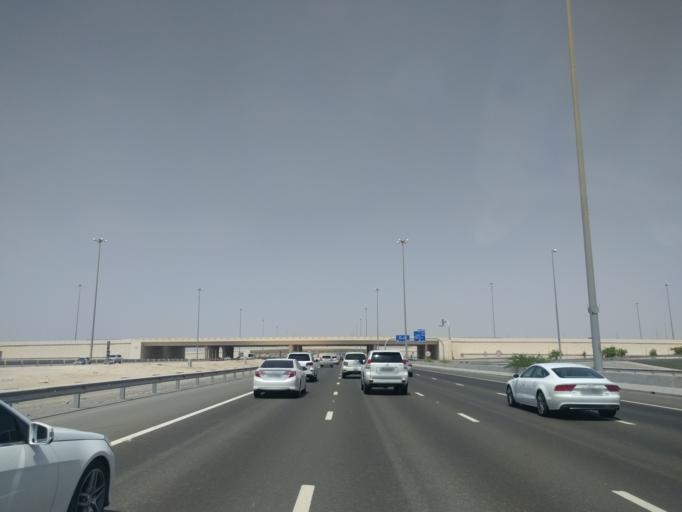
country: AE
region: Abu Dhabi
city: Abu Dhabi
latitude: 24.6921
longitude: 54.7779
